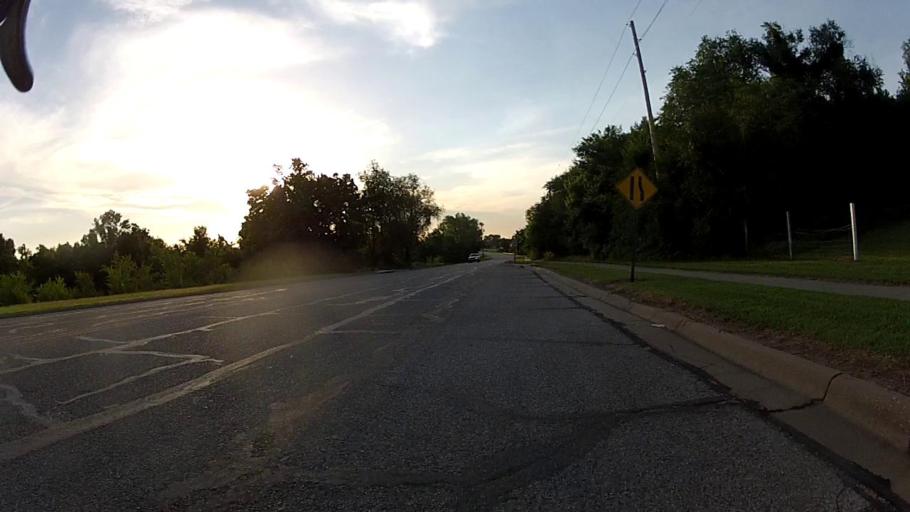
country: US
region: Kansas
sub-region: Cowley County
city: Arkansas City
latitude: 37.0857
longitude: -97.0491
